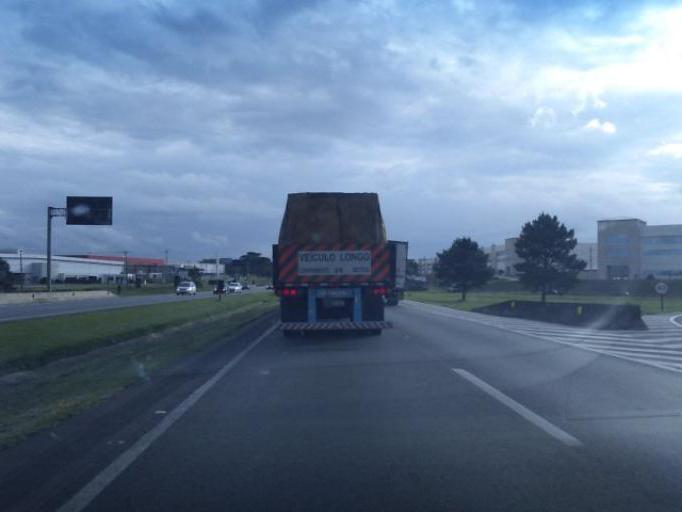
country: BR
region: Parana
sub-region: Sao Jose Dos Pinhais
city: Sao Jose dos Pinhais
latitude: -25.5127
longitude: -49.1289
